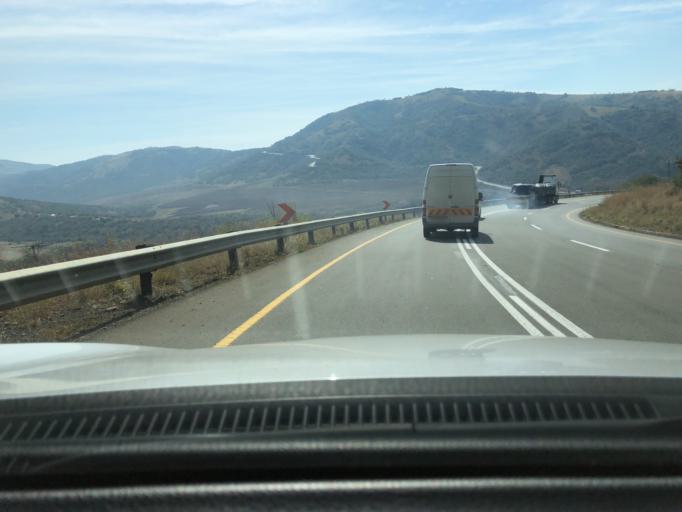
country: ZA
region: KwaZulu-Natal
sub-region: uMgungundlovu District Municipality
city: Richmond
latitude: -30.0137
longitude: 30.2384
